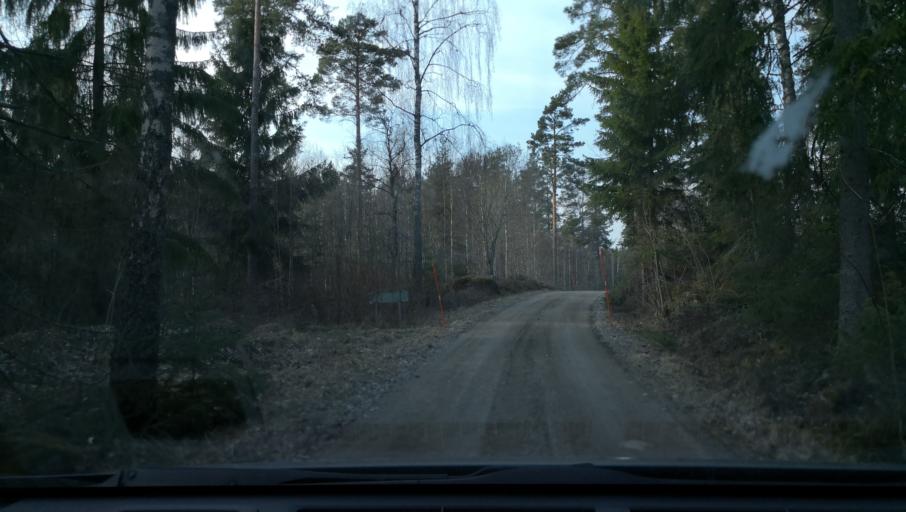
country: SE
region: OErebro
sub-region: Lindesbergs Kommun
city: Frovi
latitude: 59.3873
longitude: 15.3571
